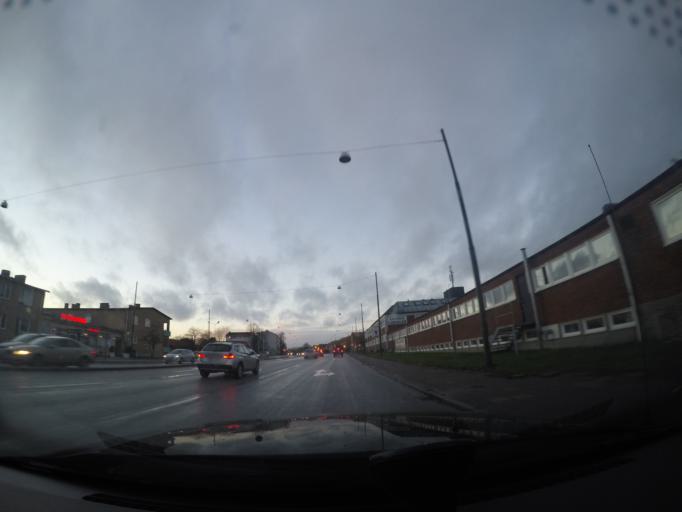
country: SE
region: Skane
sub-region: Burlovs Kommun
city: Arloev
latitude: 55.5984
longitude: 13.0472
